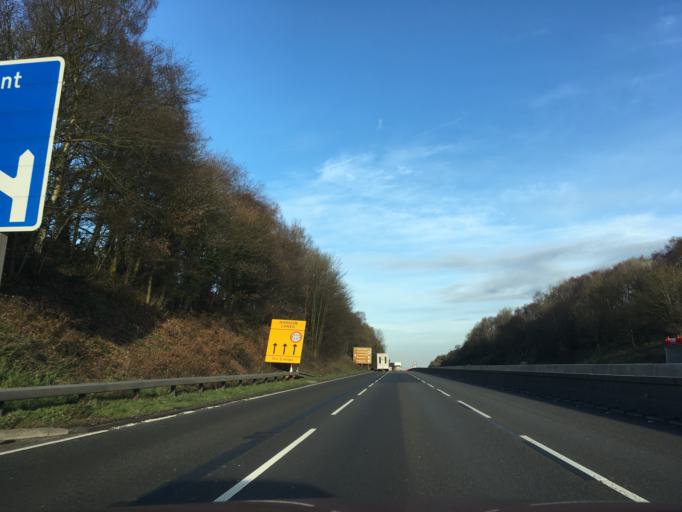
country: GB
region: England
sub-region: Staffordshire
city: Newcastle under Lyme
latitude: 52.9577
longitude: -2.2199
